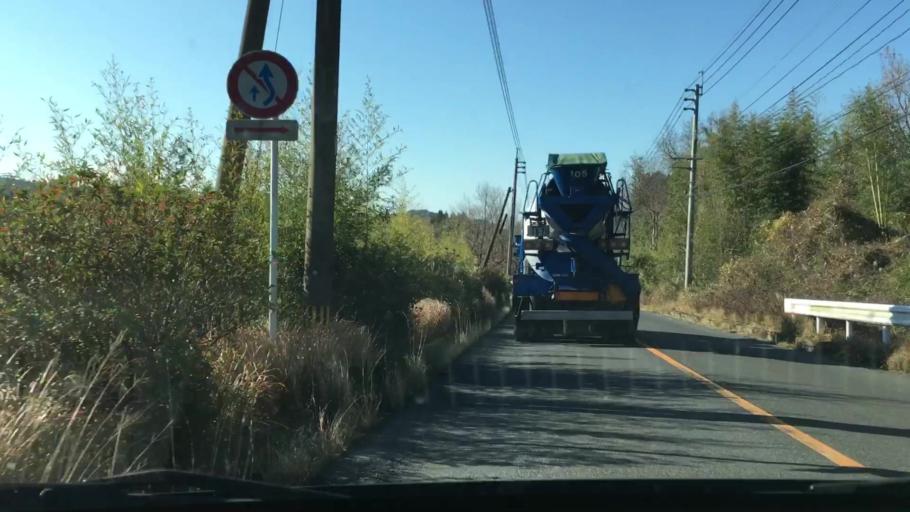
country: JP
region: Kagoshima
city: Kajiki
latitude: 31.7673
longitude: 130.6912
